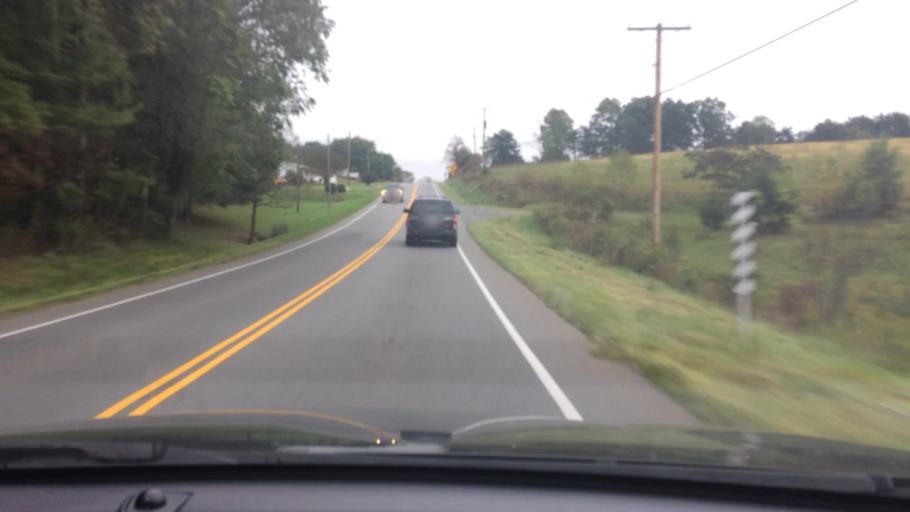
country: US
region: Virginia
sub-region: Franklin County
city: Rocky Mount
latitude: 37.0180
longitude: -79.8462
